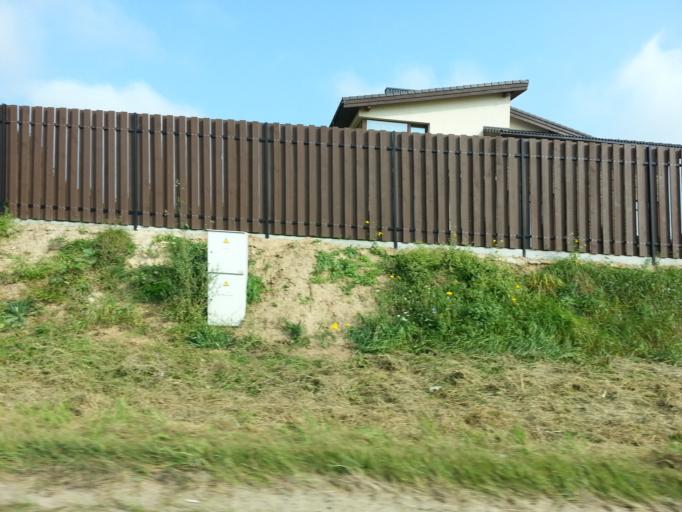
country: LT
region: Vilnius County
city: Pilaite
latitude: 54.7155
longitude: 25.1344
